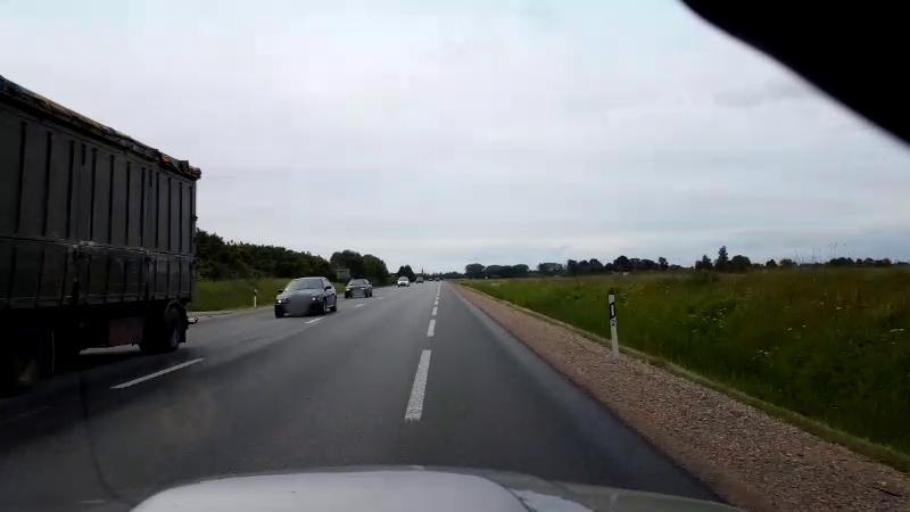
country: LV
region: Lecava
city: Iecava
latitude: 56.6169
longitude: 24.2167
